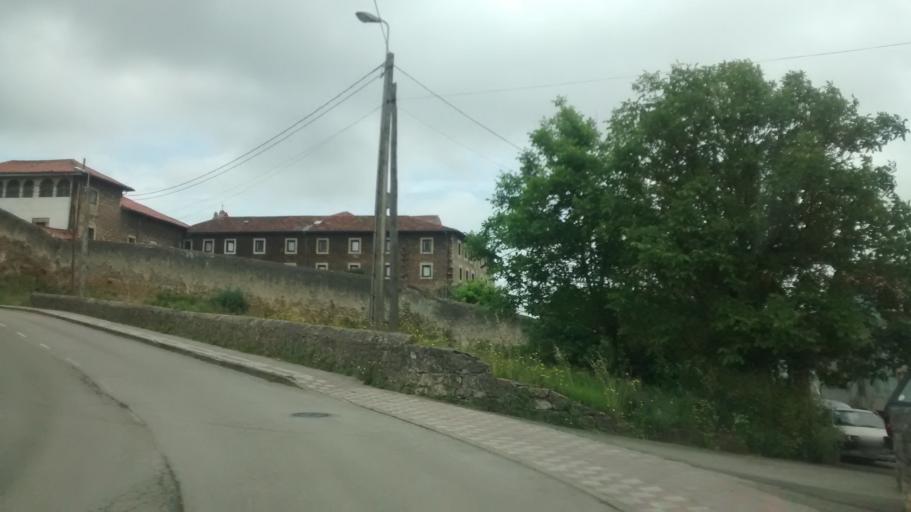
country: ES
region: Cantabria
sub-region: Provincia de Cantabria
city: El Astillero
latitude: 43.4189
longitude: -3.8288
